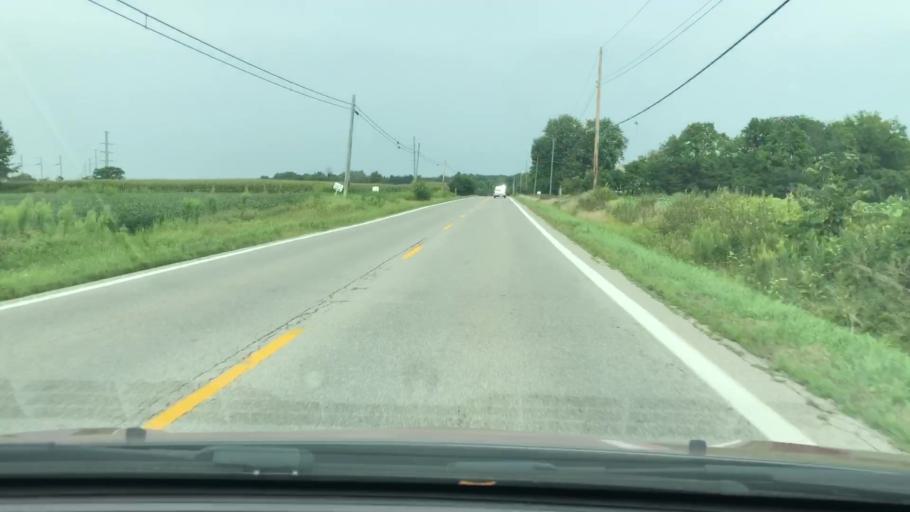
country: US
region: Ohio
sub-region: Delaware County
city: Sunbury
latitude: 40.2319
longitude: -82.8327
